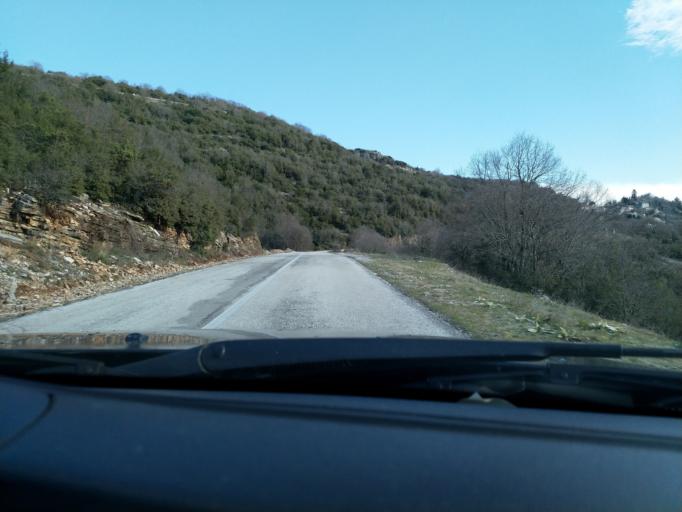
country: GR
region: Epirus
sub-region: Nomos Ioanninon
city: Asprangeloi
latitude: 39.8703
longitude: 20.7412
